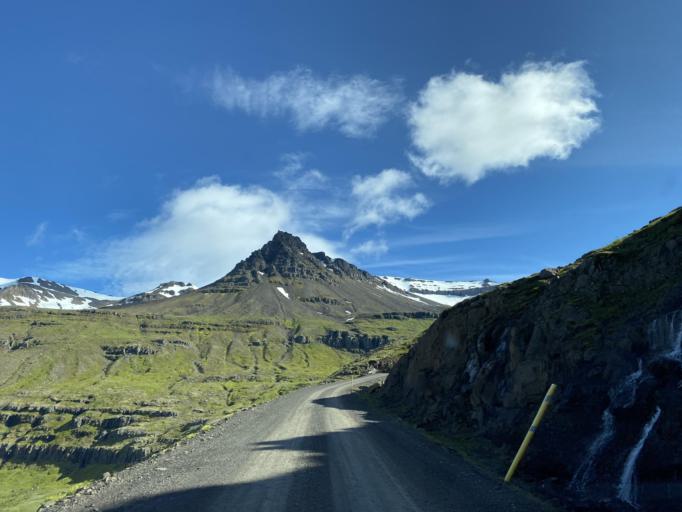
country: IS
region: East
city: Eskifjoerdur
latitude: 65.1808
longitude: -14.0851
